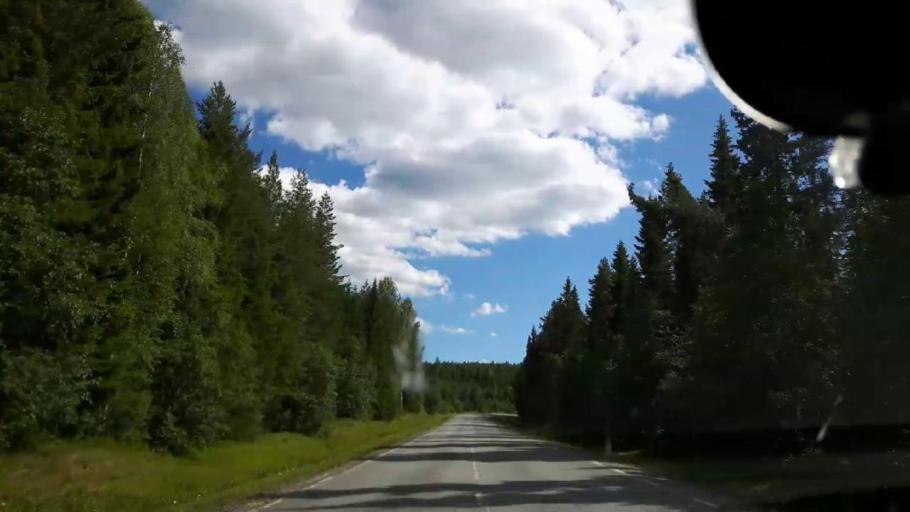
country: SE
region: Vaesternorrland
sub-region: Ange Kommun
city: Fransta
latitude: 62.8143
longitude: 16.2080
